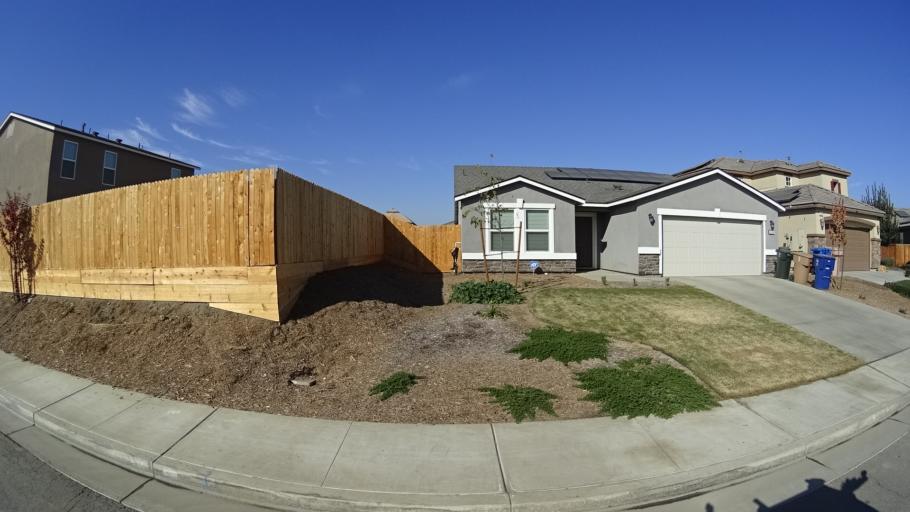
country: US
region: California
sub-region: Kern County
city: Greenfield
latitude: 35.2799
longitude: -119.0666
